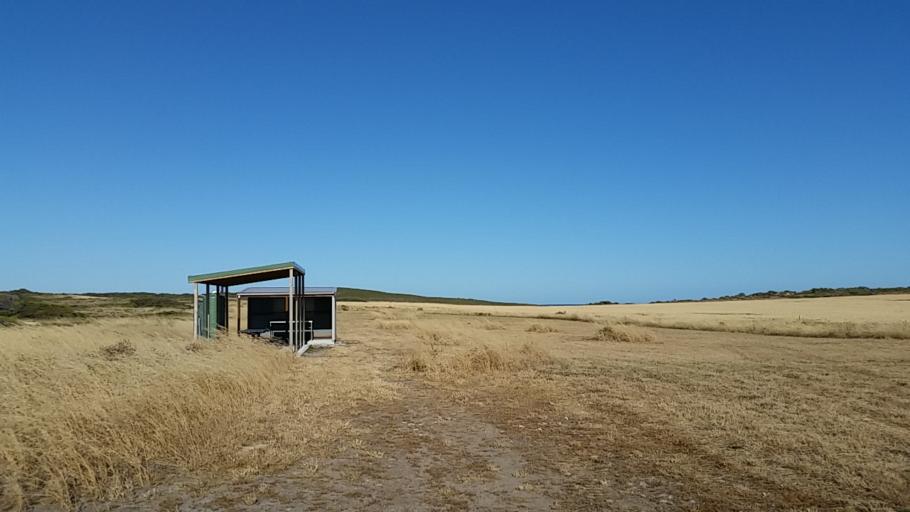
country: AU
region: South Australia
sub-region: Yorke Peninsula
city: Honiton
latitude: -35.2398
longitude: 137.1404
